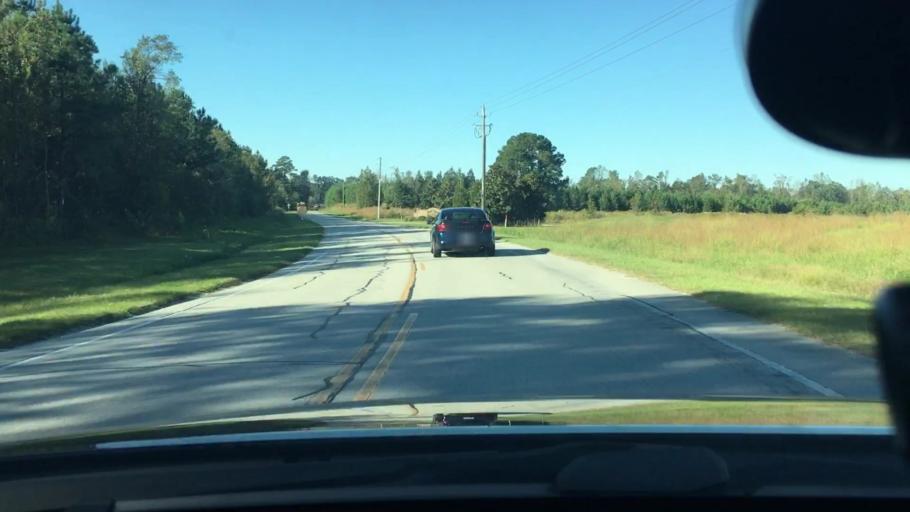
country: US
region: North Carolina
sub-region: Craven County
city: Vanceboro
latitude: 35.2800
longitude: -77.1529
